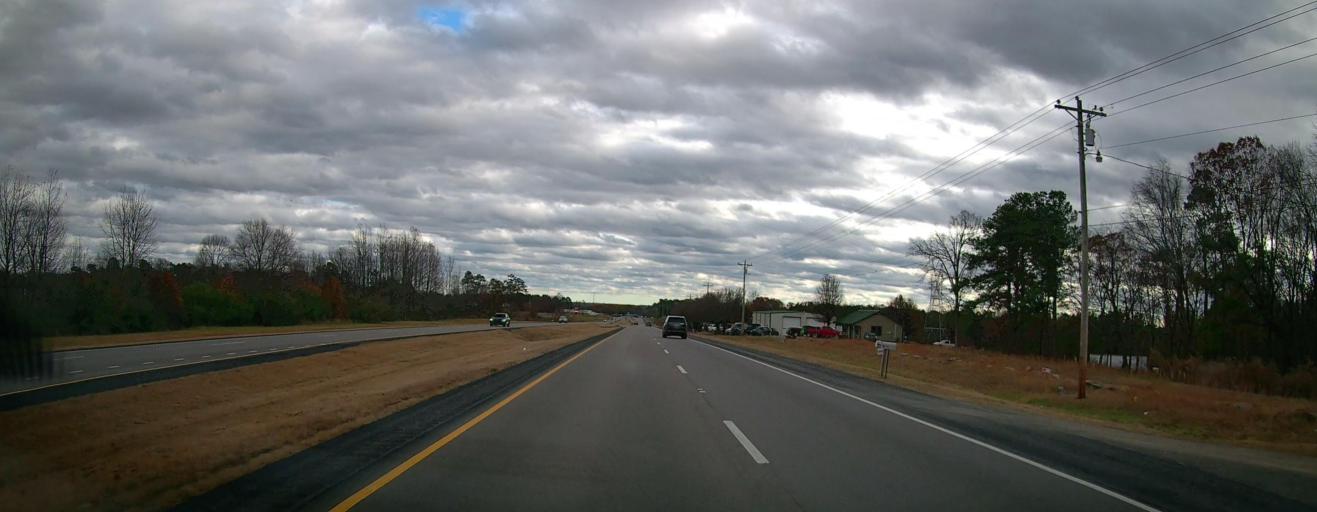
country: US
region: Alabama
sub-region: Morgan County
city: Falkville
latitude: 34.2764
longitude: -86.9946
